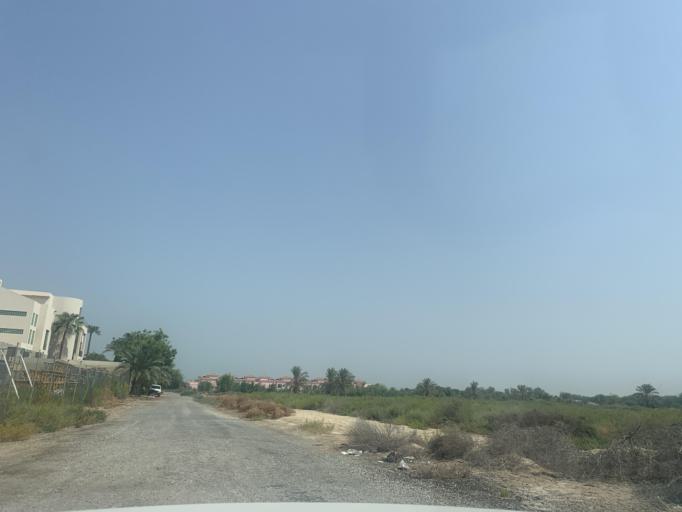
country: BH
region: Central Governorate
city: Madinat Hamad
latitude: 26.1650
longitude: 50.4595
